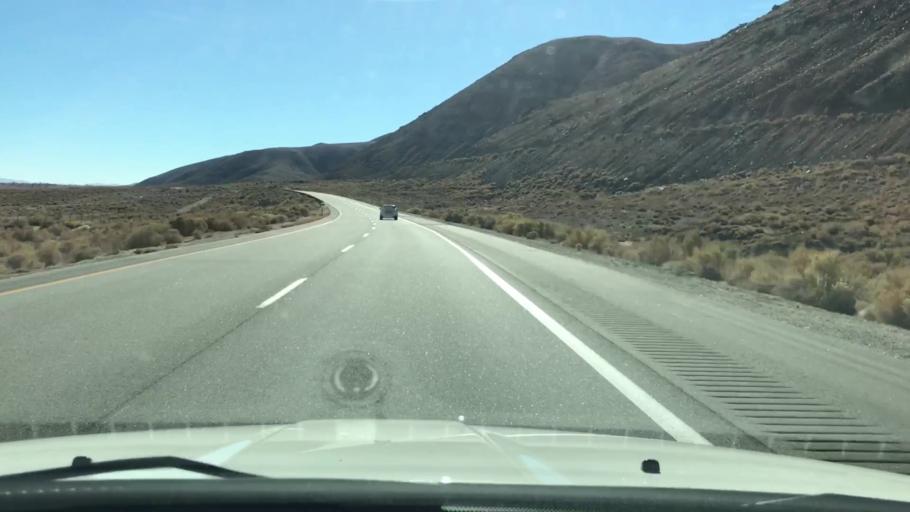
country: US
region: California
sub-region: Inyo County
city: Lone Pine
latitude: 36.6589
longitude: -118.0950
